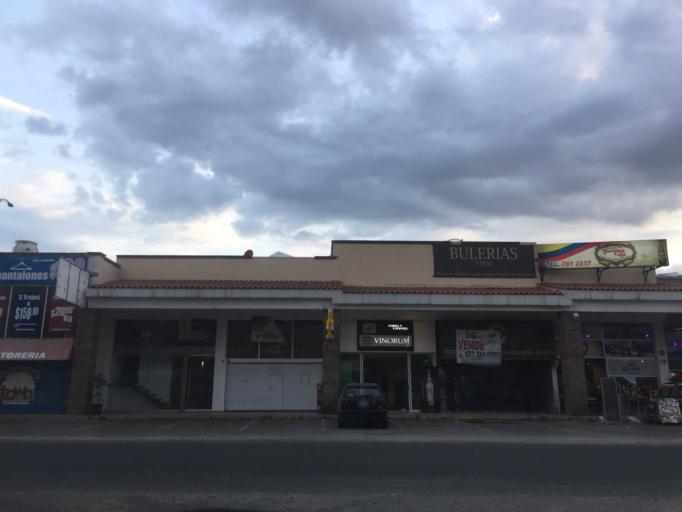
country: MX
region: Guanajuato
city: Leon
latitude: 21.1689
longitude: -101.6924
